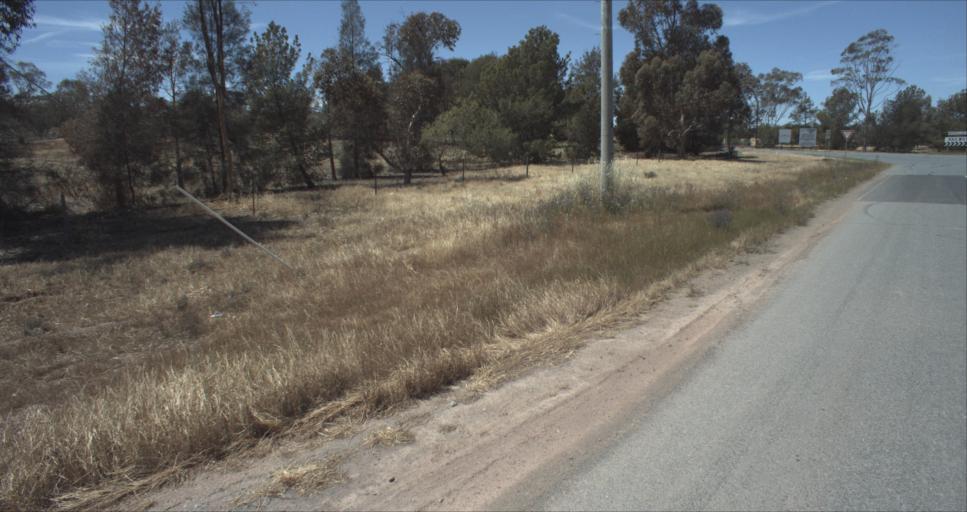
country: AU
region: New South Wales
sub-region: Leeton
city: Leeton
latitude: -34.6464
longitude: 146.4721
